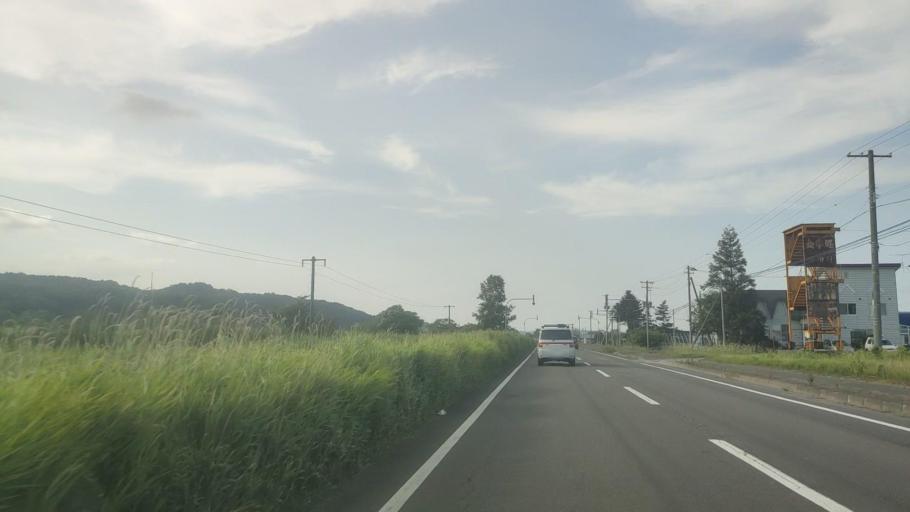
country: JP
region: Hokkaido
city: Iwamizawa
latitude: 42.9889
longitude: 141.7915
